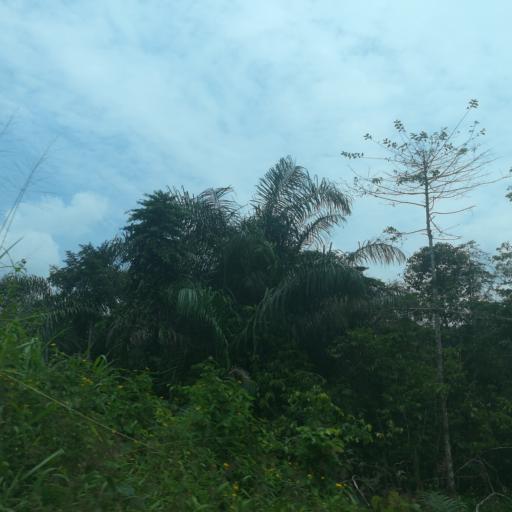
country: NG
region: Lagos
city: Ejirin
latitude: 6.6624
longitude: 3.8133
